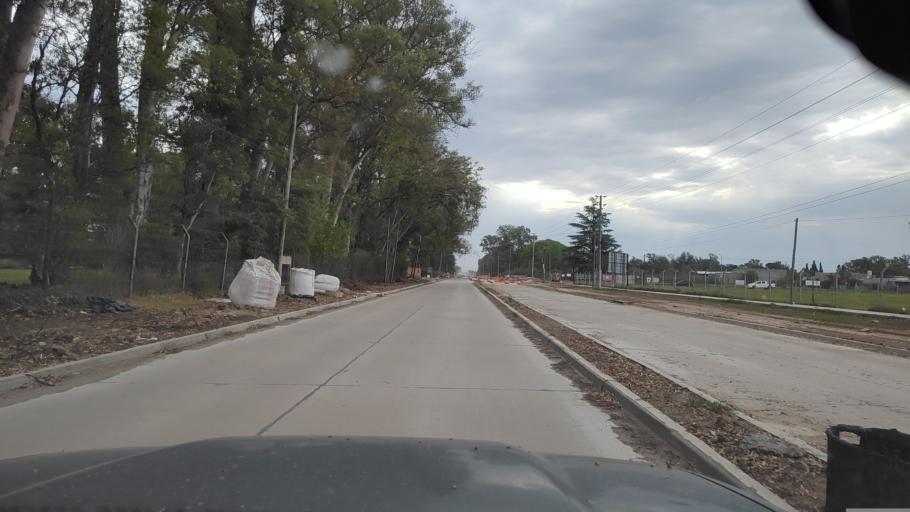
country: AR
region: Buenos Aires
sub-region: Partido de Lujan
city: Lujan
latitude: -34.5517
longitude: -59.0903
